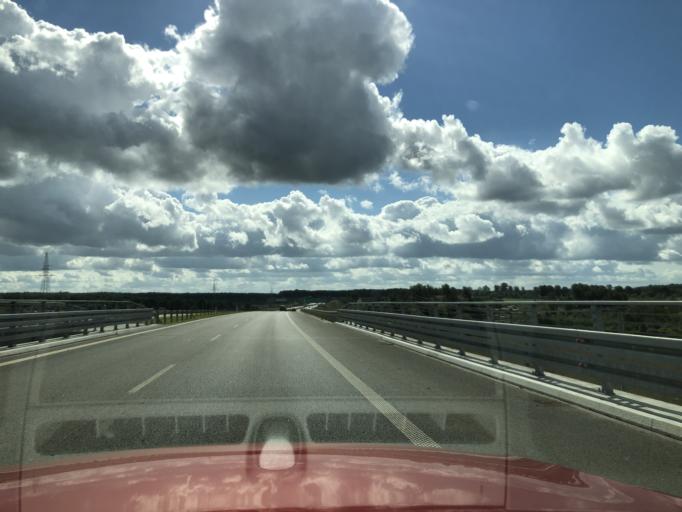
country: PL
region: West Pomeranian Voivodeship
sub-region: Powiat szczecinecki
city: Szczecinek
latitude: 53.7023
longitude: 16.7288
